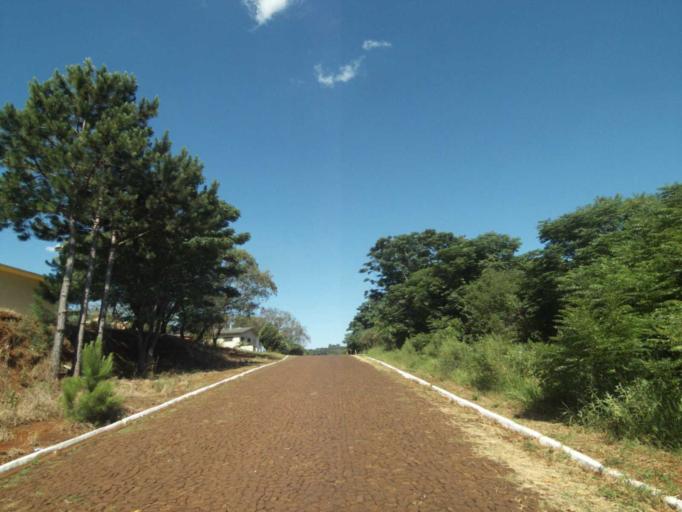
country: BR
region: Parana
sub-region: Laranjeiras Do Sul
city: Laranjeiras do Sul
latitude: -25.3827
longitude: -52.2014
